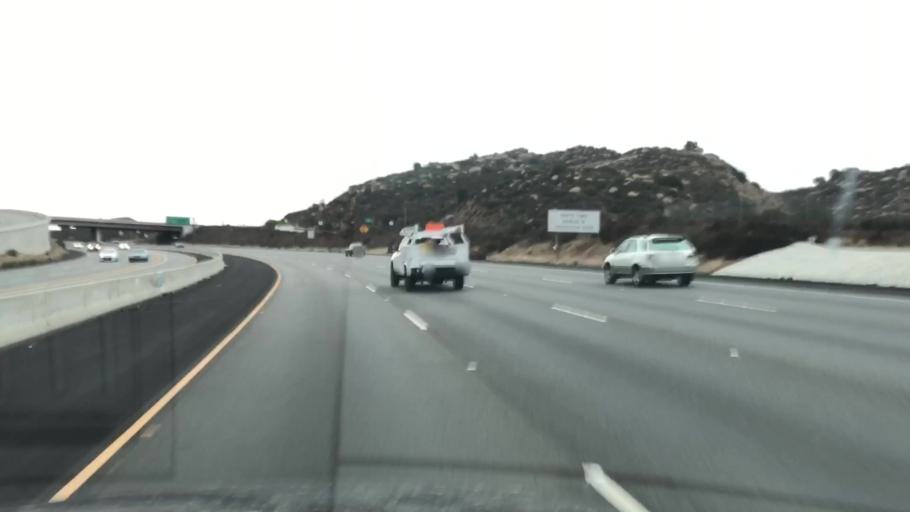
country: US
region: California
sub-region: Los Angeles County
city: Chatsworth
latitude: 34.2666
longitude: -118.6384
